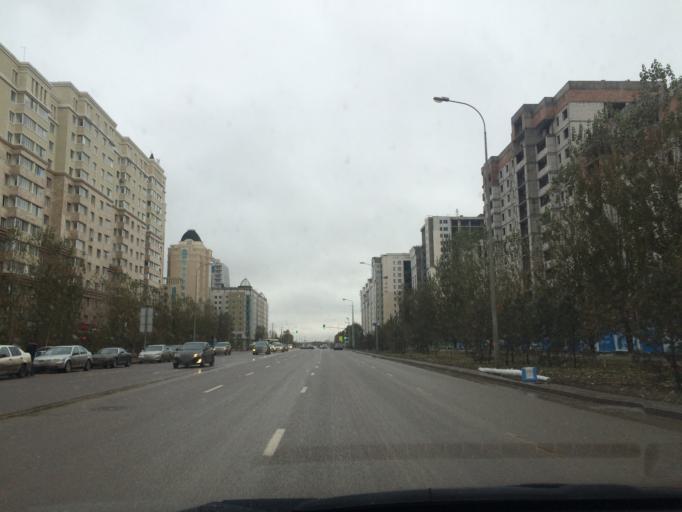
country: KZ
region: Astana Qalasy
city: Astana
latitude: 51.1134
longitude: 71.4302
